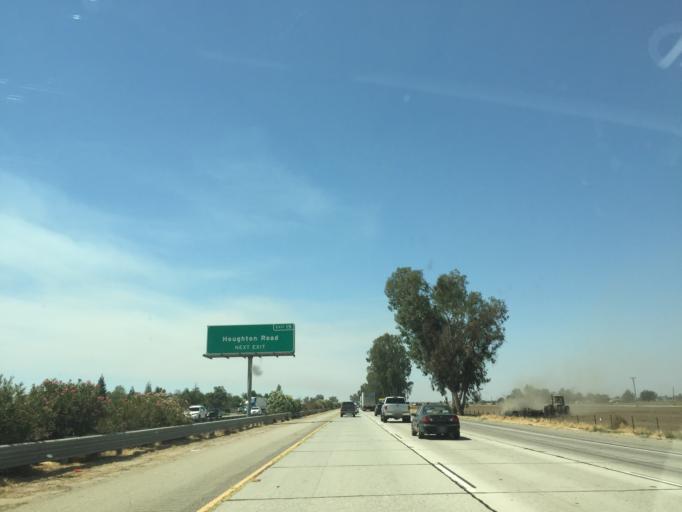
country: US
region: California
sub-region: Kern County
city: Greenfield
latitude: 35.2258
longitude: -119.0129
